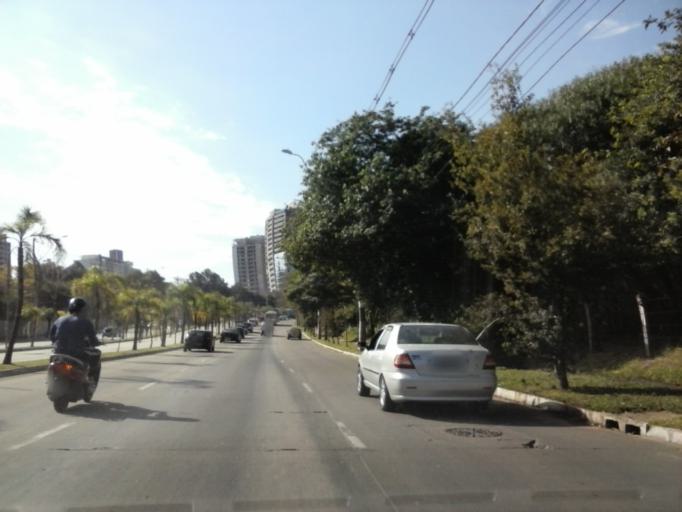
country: BR
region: Rio Grande do Sul
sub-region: Porto Alegre
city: Porto Alegre
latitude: -30.0467
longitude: -51.1778
